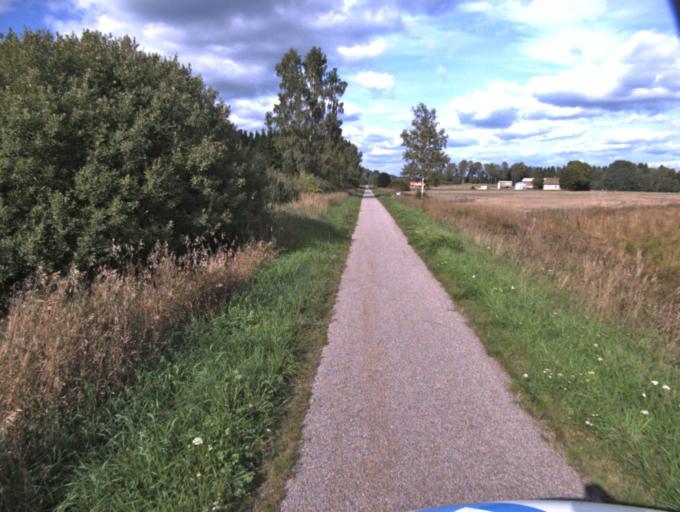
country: SE
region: Vaestra Goetaland
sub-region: Ulricehamns Kommun
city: Ulricehamn
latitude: 57.8782
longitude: 13.4292
